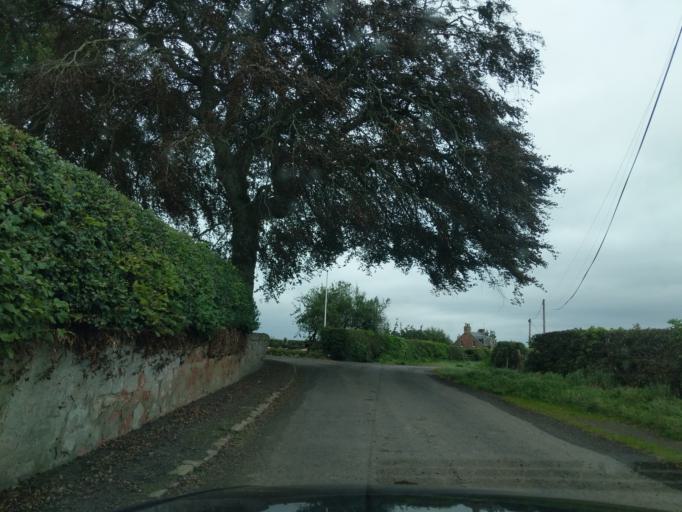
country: GB
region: Scotland
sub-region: The Scottish Borders
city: Kelso
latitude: 55.5980
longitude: -2.5154
